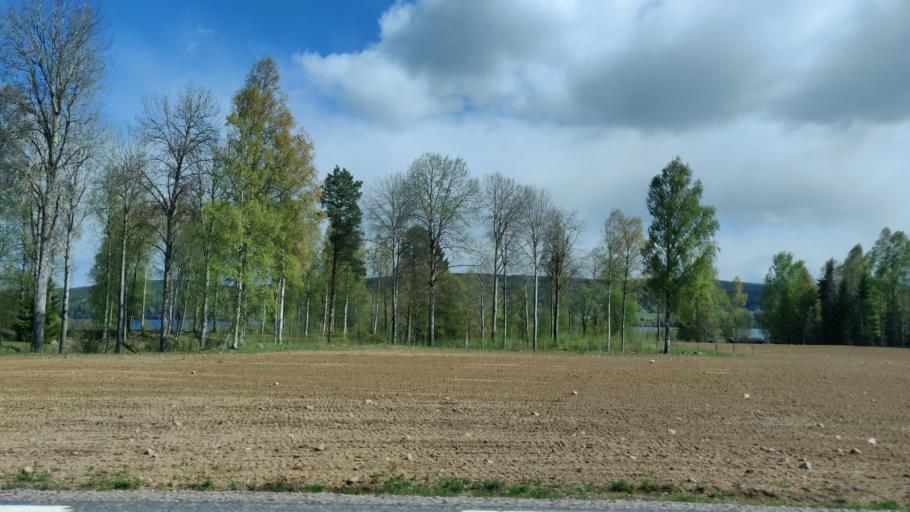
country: SE
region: Vaermland
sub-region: Munkfors Kommun
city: Munkfors
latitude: 59.8532
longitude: 13.7081
